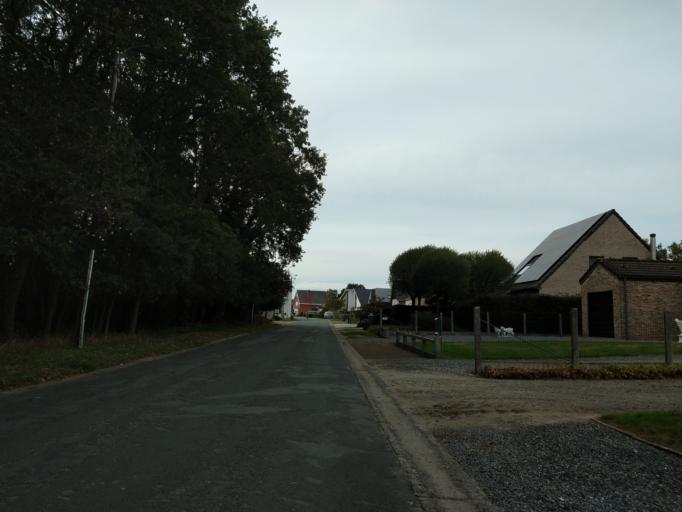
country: BE
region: Flanders
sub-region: Provincie Vlaams-Brabant
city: Haacht
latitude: 50.9817
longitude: 4.6470
